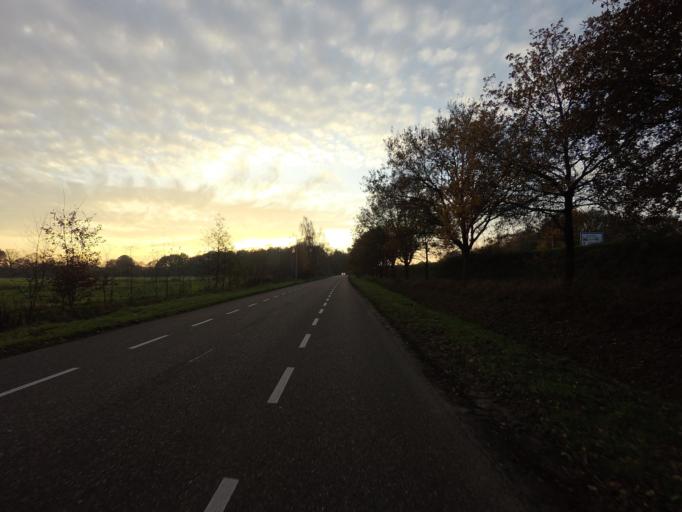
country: NL
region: North Brabant
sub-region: Gemeente Breda
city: Breda
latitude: 51.5281
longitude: 4.7730
